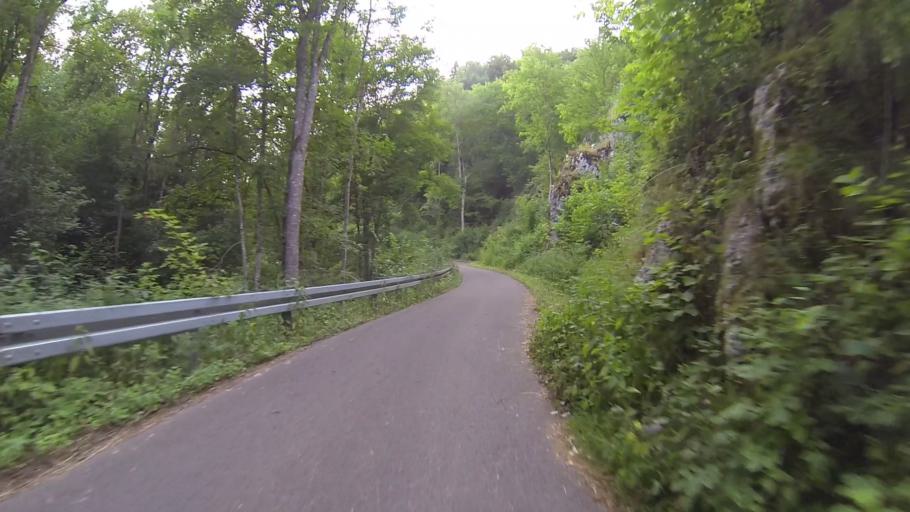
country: DE
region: Baden-Wuerttemberg
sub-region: Tuebingen Region
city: Blaubeuren
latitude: 48.4497
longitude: 9.8520
